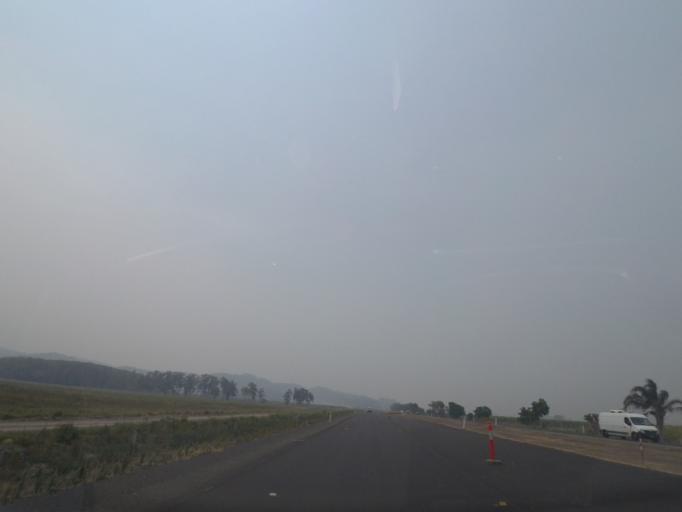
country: AU
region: New South Wales
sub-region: Ballina
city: Ballina
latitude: -28.8948
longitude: 153.4812
